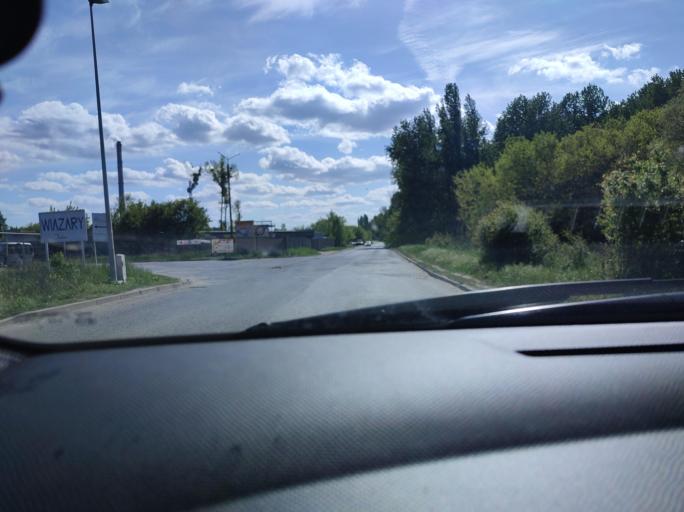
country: PL
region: West Pomeranian Voivodeship
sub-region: Powiat policki
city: Police
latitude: 53.5840
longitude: 14.5380
